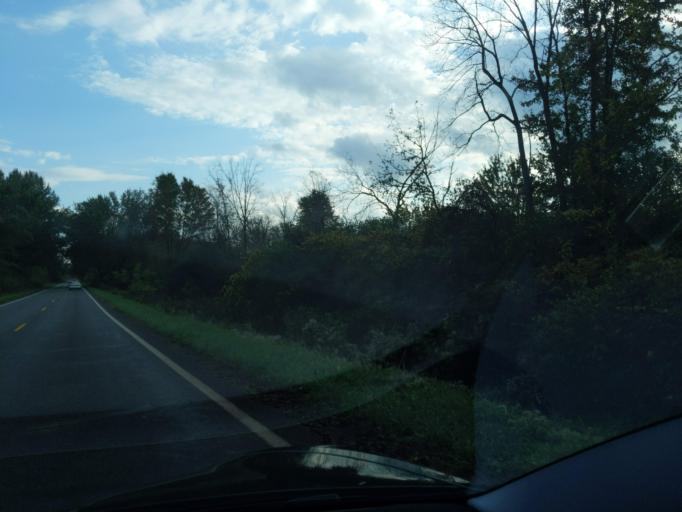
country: US
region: Michigan
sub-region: Jackson County
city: Jackson
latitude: 42.2970
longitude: -84.4626
